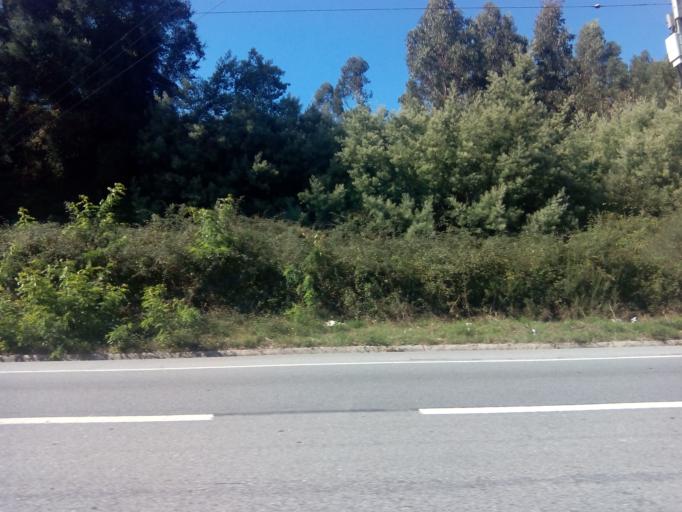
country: PT
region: Porto
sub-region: Paredes
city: Baltar
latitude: 41.1891
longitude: -8.3678
